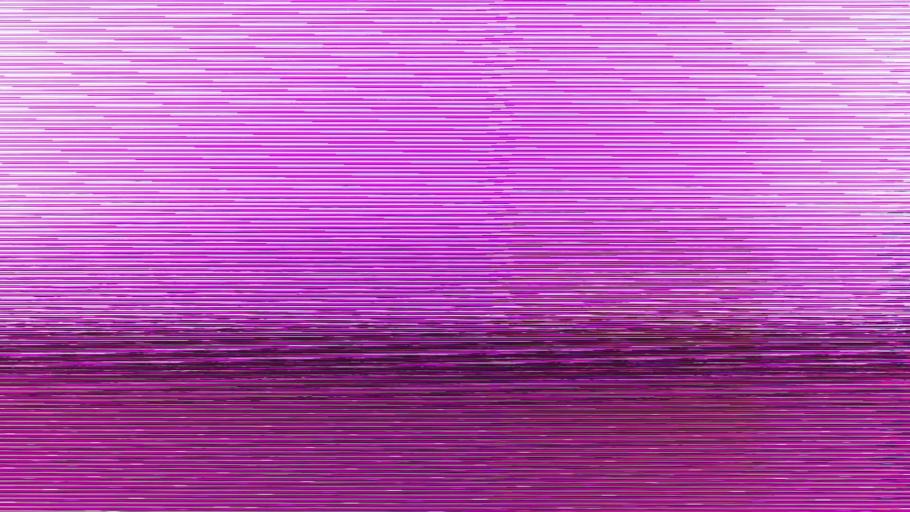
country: US
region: Michigan
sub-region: Wayne County
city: Belleville
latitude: 42.2192
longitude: -83.5164
